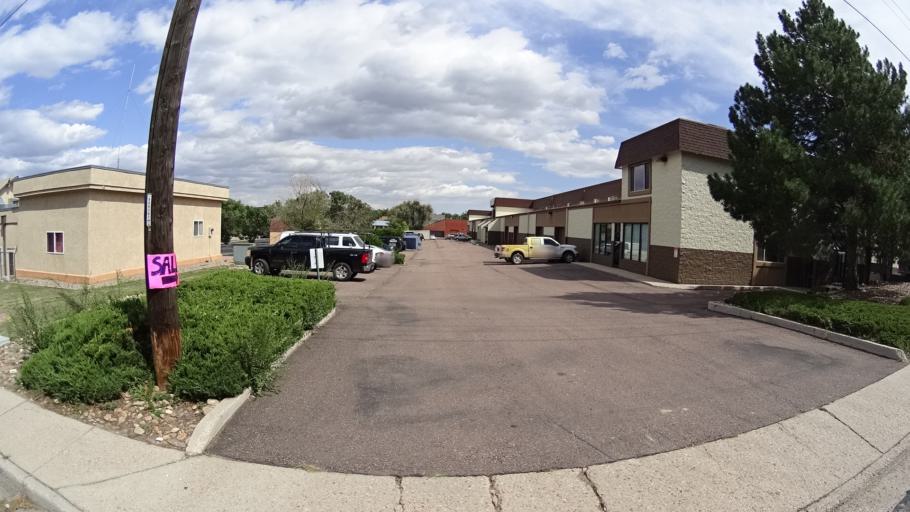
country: US
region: Colorado
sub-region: El Paso County
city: Cimarron Hills
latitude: 38.8850
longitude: -104.7608
